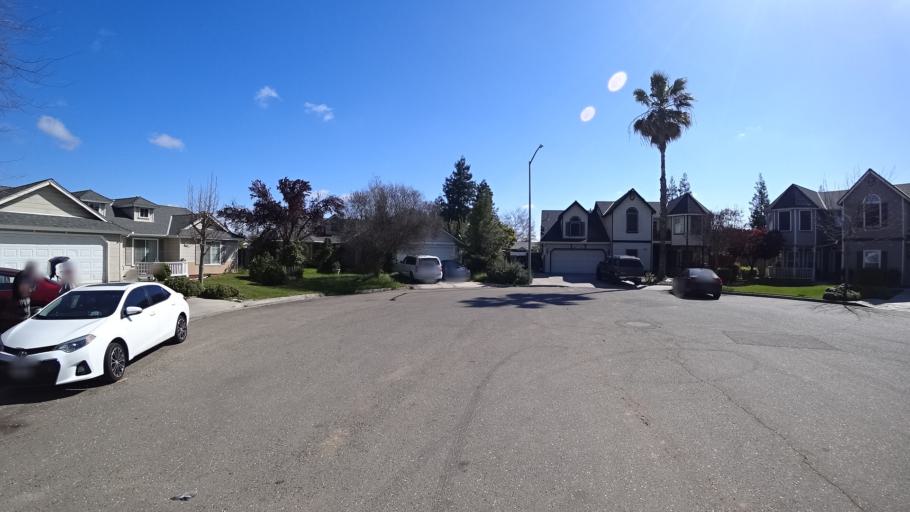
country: US
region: California
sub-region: Fresno County
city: West Park
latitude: 36.7904
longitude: -119.8879
